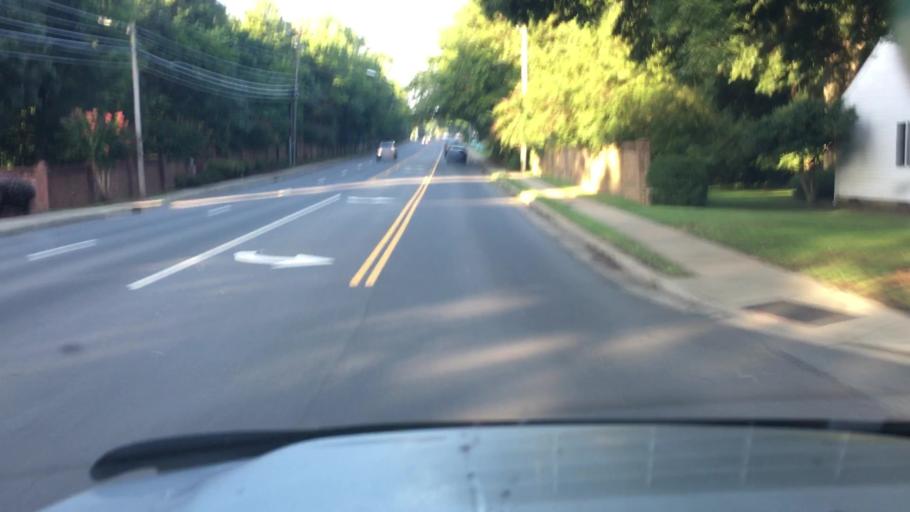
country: US
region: North Carolina
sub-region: Mecklenburg County
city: Pineville
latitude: 35.1189
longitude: -80.8211
